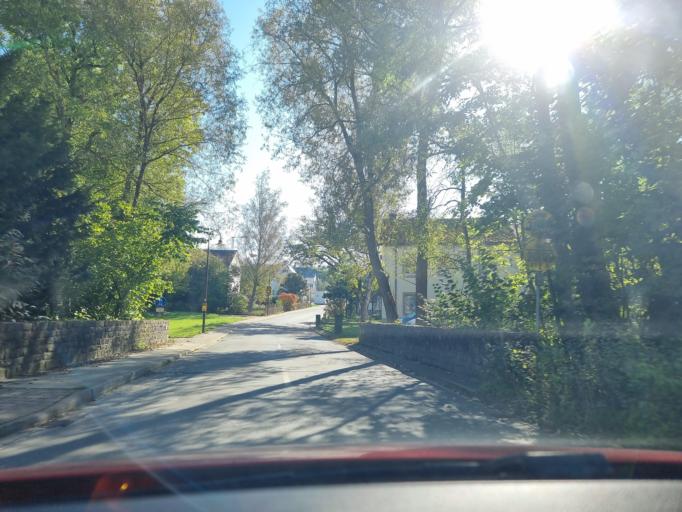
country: DE
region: Rheinland-Pfalz
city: Trierweiler
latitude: 49.7571
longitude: 6.5549
